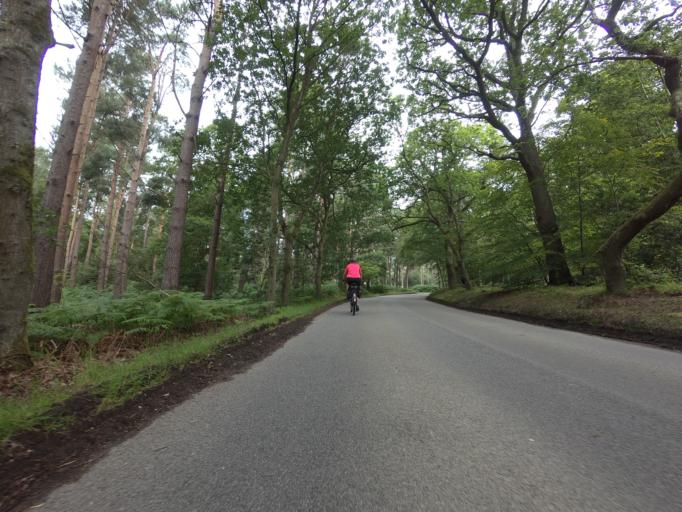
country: GB
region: Scotland
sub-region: Moray
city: Elgin
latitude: 57.6533
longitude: -3.3451
